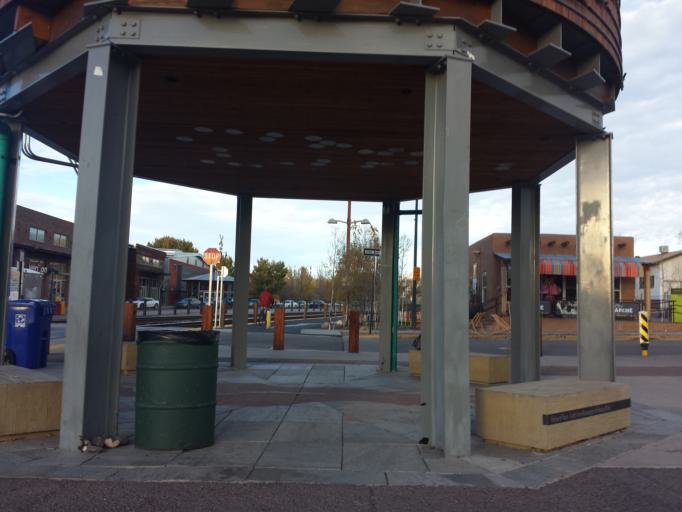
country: US
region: New Mexico
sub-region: Santa Fe County
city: Santa Fe
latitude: 35.6829
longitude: -105.9487
